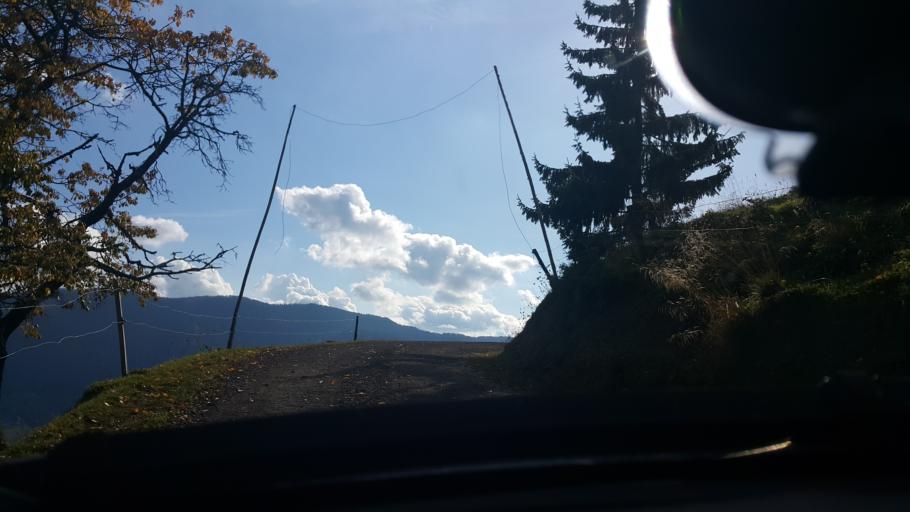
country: SI
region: Mislinja
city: Mislinja
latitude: 46.4297
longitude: 15.2554
